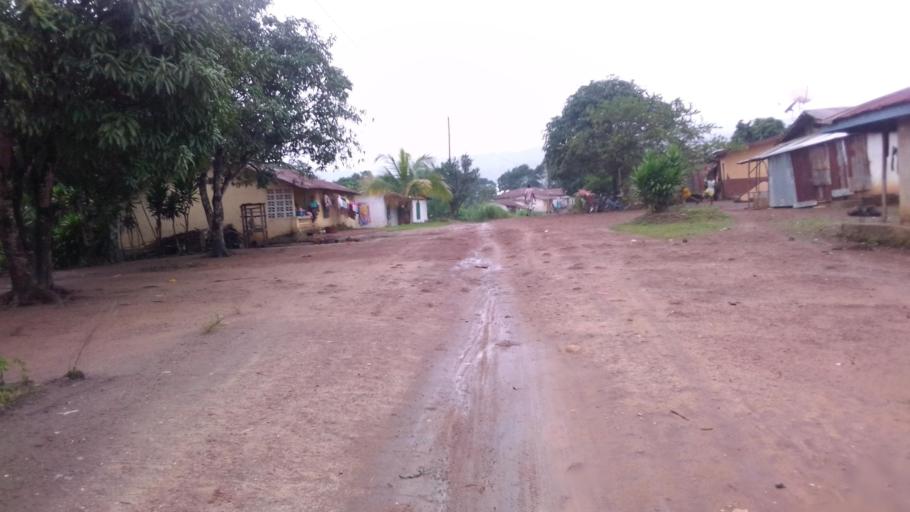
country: SL
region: Eastern Province
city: Kenema
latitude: 7.8865
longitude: -11.1716
